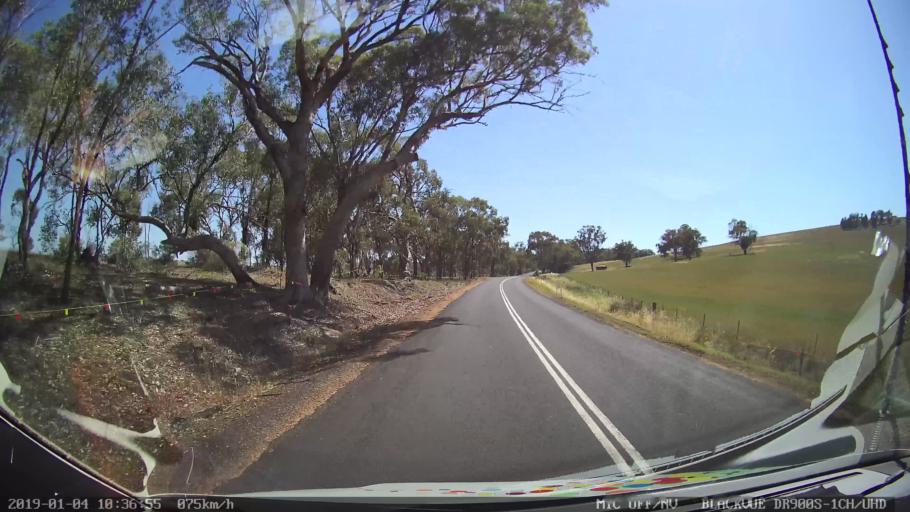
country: AU
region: New South Wales
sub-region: Cabonne
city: Canowindra
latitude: -33.2999
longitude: 148.6893
